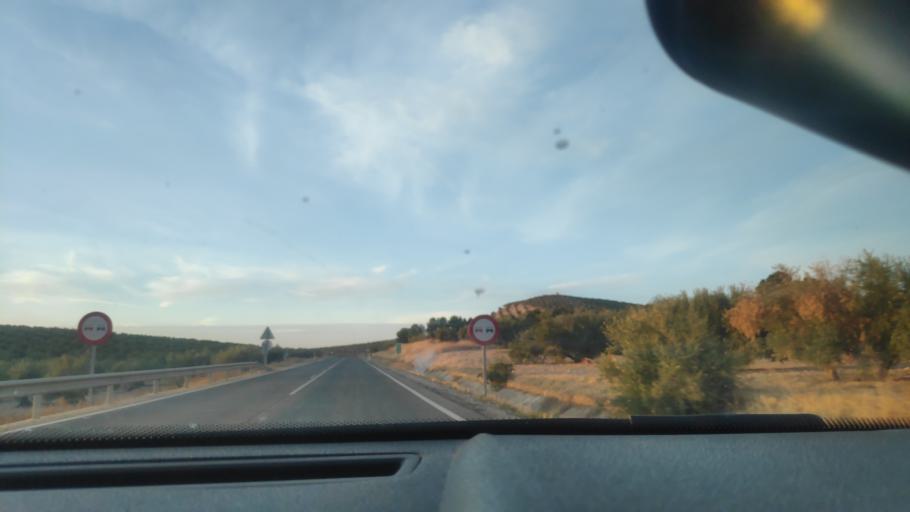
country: ES
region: Andalusia
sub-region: Provincia de Jaen
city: Villardompardo
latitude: 37.8207
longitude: -4.0410
